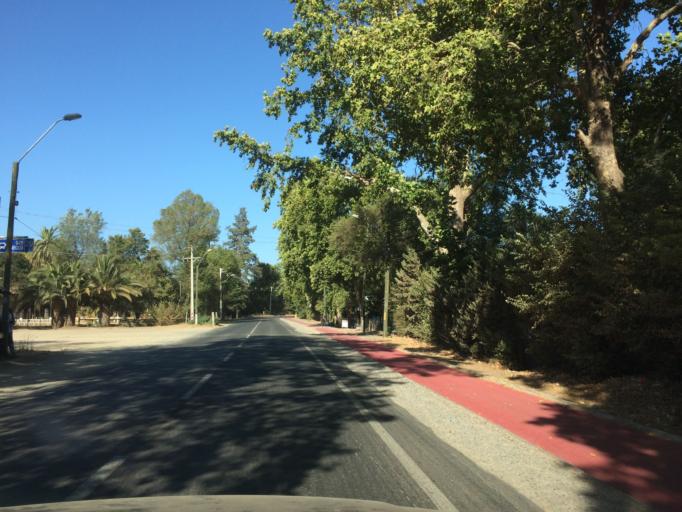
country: CL
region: Santiago Metropolitan
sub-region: Provincia de Melipilla
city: Melipilla
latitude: -33.4892
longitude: -71.1866
